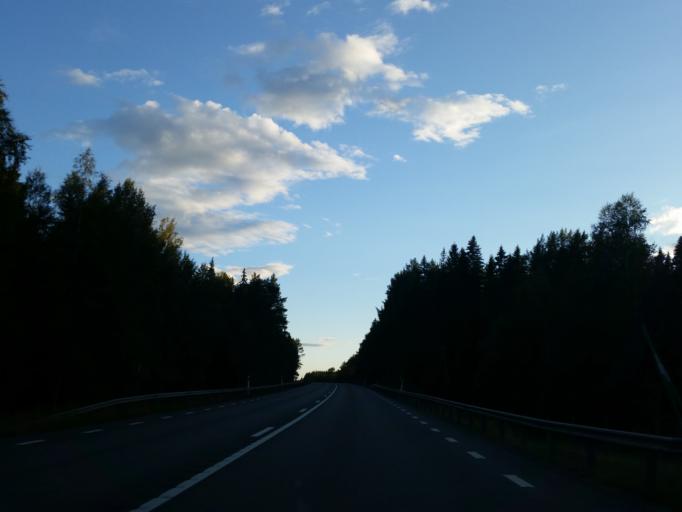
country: SE
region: Vaesterbotten
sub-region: Robertsfors Kommun
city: Robertsfors
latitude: 64.0113
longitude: 20.8142
